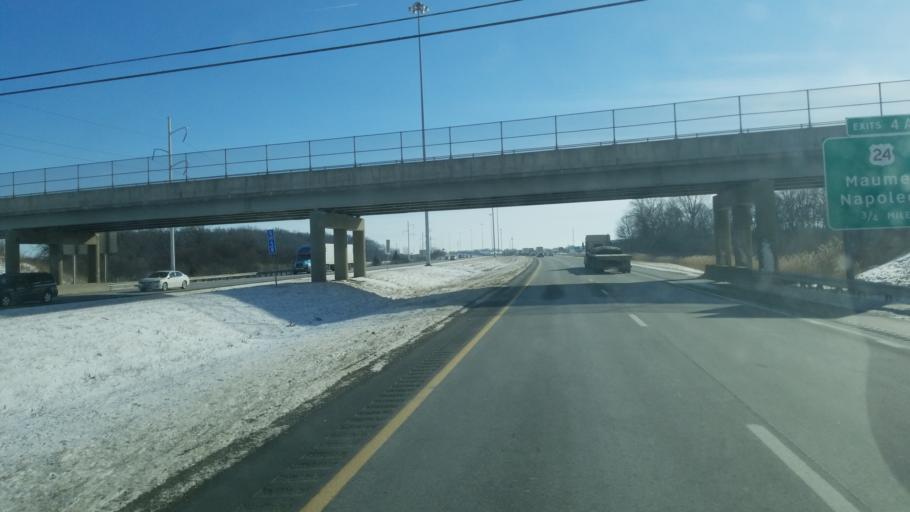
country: US
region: Ohio
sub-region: Lucas County
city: Maumee
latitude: 41.5721
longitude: -83.6914
